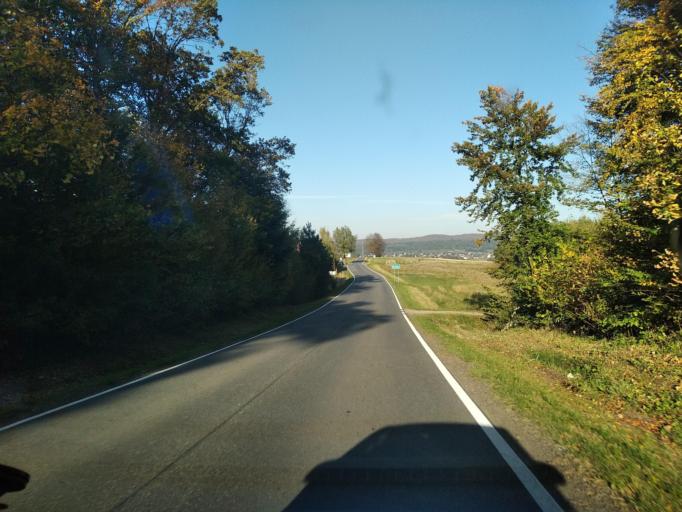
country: PL
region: Subcarpathian Voivodeship
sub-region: Powiat brzozowski
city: Turze Pole
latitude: 49.6653
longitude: 22.0168
